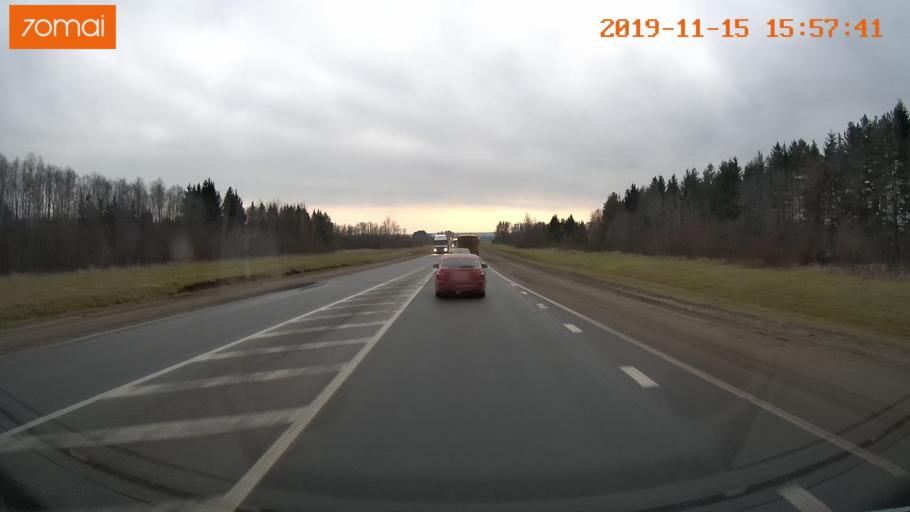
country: RU
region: Jaroslavl
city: Yaroslavl
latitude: 57.8276
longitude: 39.9612
